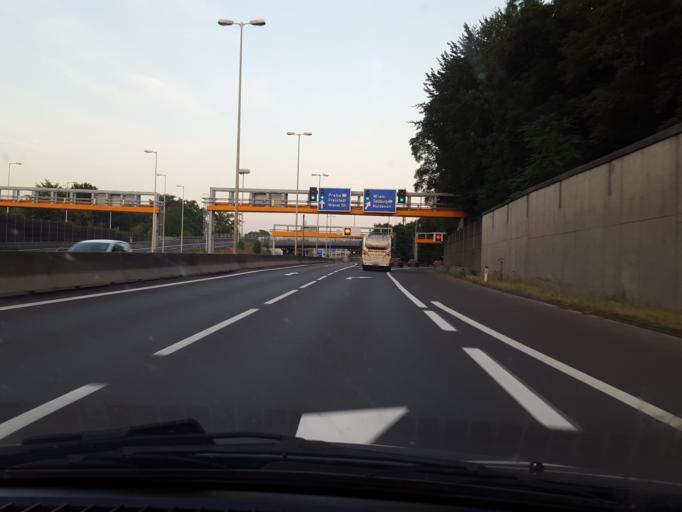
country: AT
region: Upper Austria
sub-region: Linz Stadt
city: Linz
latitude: 48.2799
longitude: 14.2911
